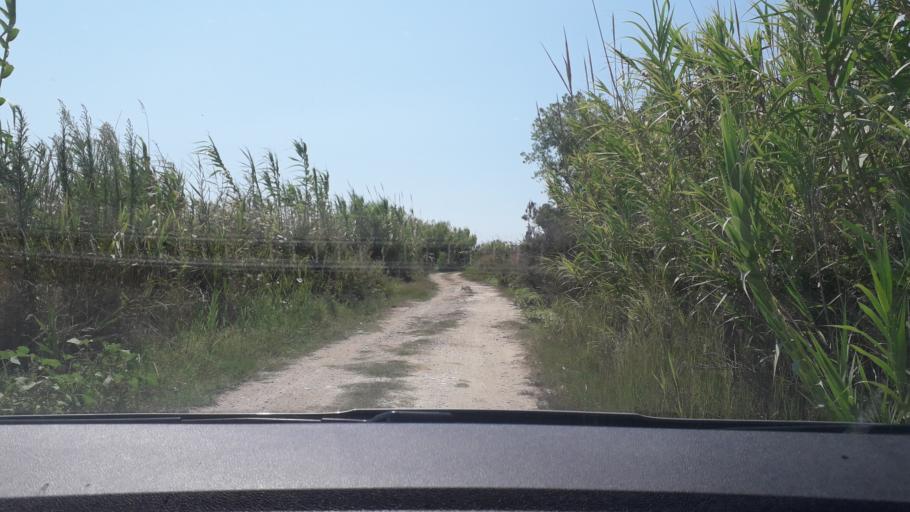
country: GR
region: Ionian Islands
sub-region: Nomos Kerkyras
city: Agios Matthaios
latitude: 39.4552
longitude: 19.8843
